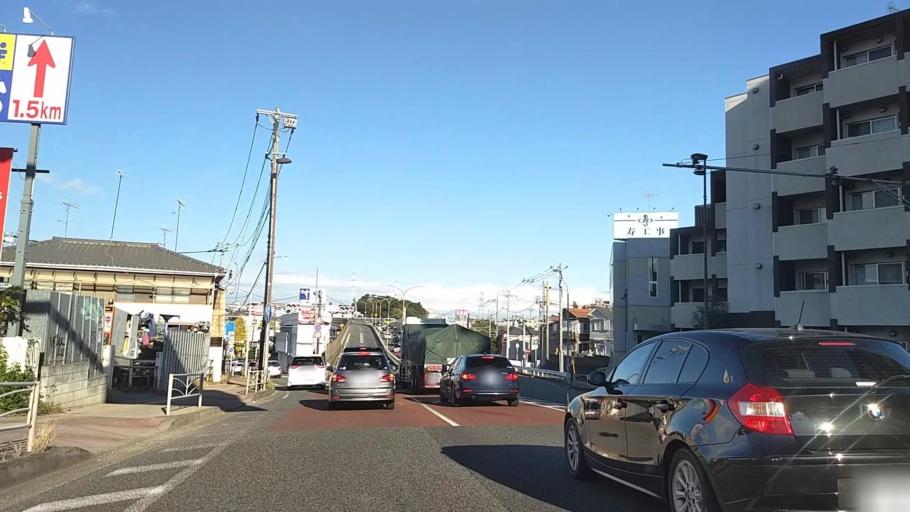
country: JP
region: Tokyo
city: Chofugaoka
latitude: 35.5808
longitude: 139.5939
